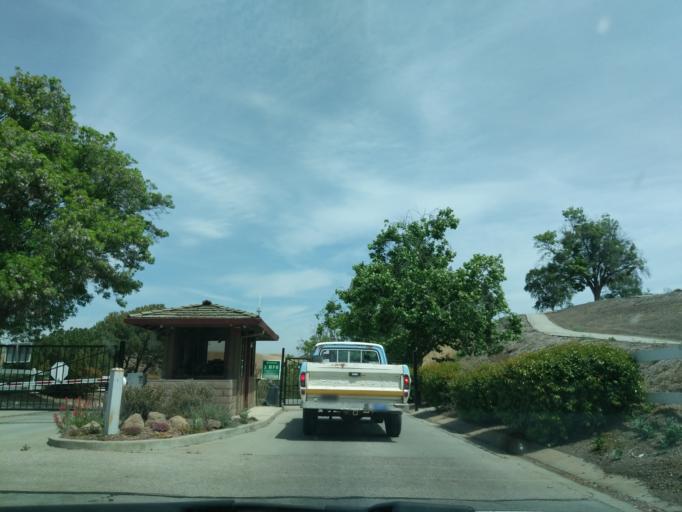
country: US
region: California
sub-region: San Benito County
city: Ridgemark
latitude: 36.8090
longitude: -121.3478
